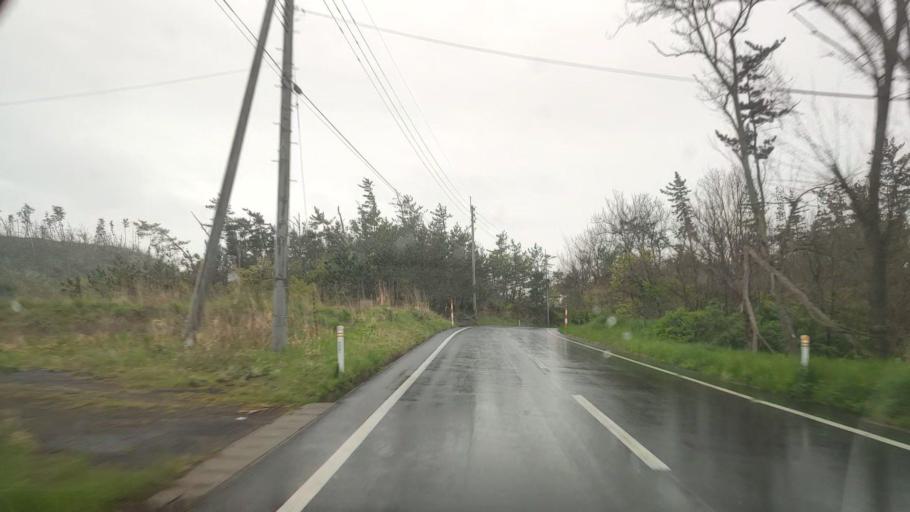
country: JP
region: Akita
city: Noshiromachi
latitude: 40.0797
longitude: 139.9541
